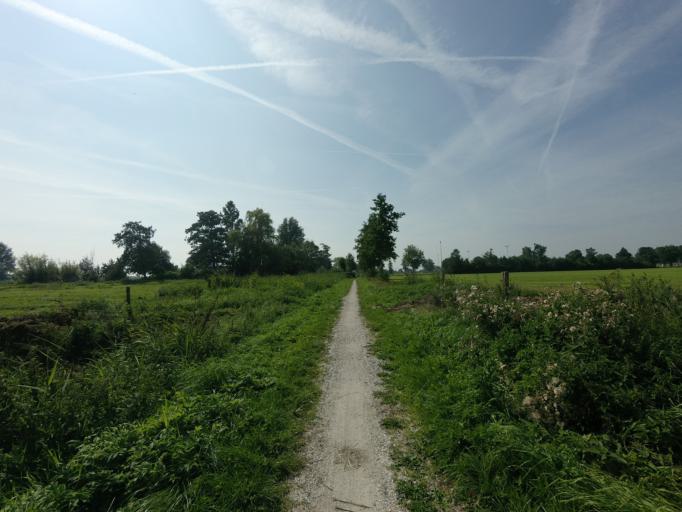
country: NL
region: Friesland
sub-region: Gemeente Lemsterland
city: Echtenerbrug
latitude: 52.8436
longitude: 5.8831
